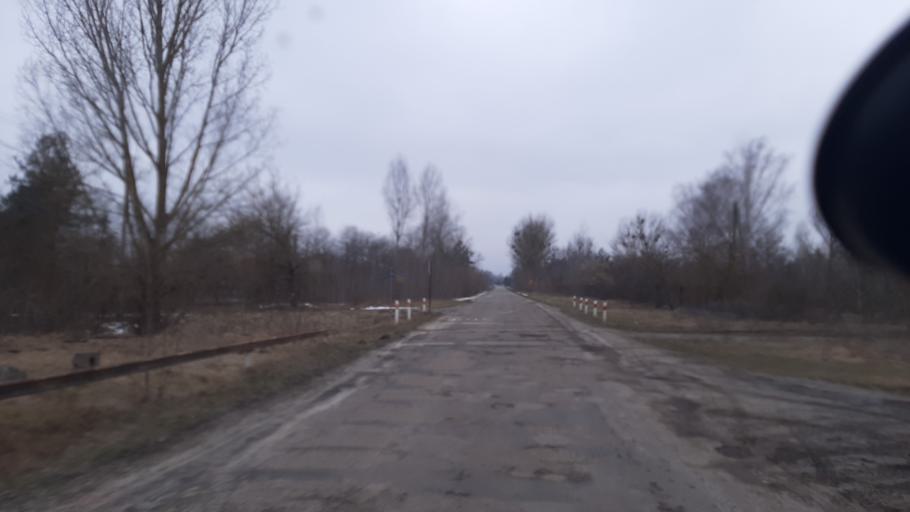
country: PL
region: Lublin Voivodeship
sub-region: Powiat wlodawski
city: Wlodawa
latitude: 51.5195
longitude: 23.5880
